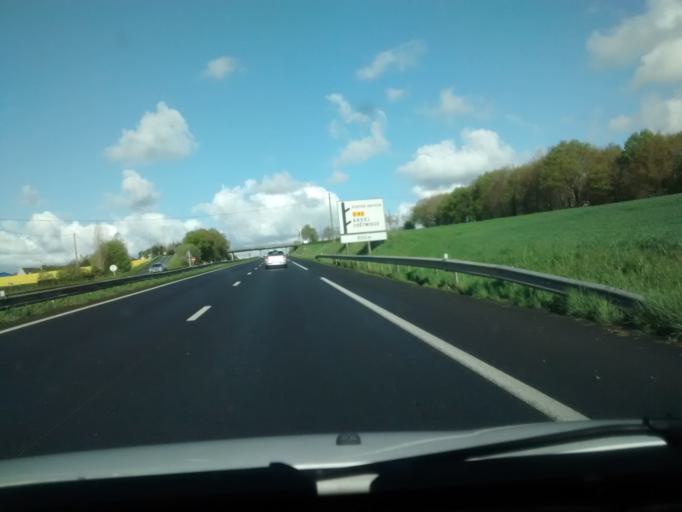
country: FR
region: Brittany
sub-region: Departement des Cotes-d'Armor
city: Coetmieux
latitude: 48.4749
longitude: -2.5705
